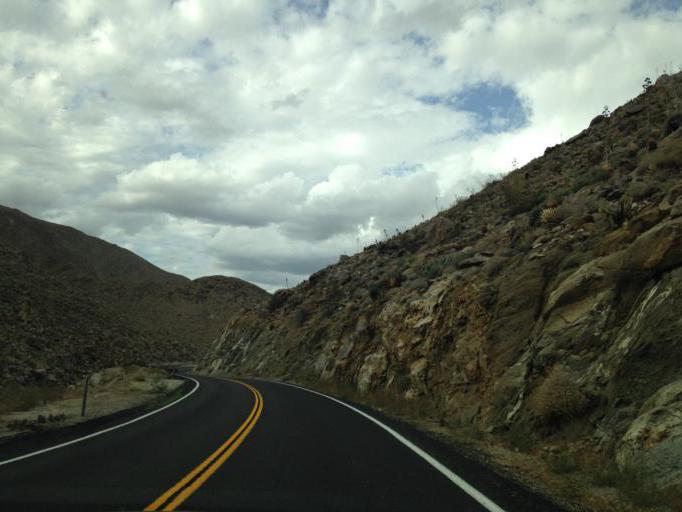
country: US
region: California
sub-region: San Diego County
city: Borrego Springs
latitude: 33.1208
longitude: -116.4343
